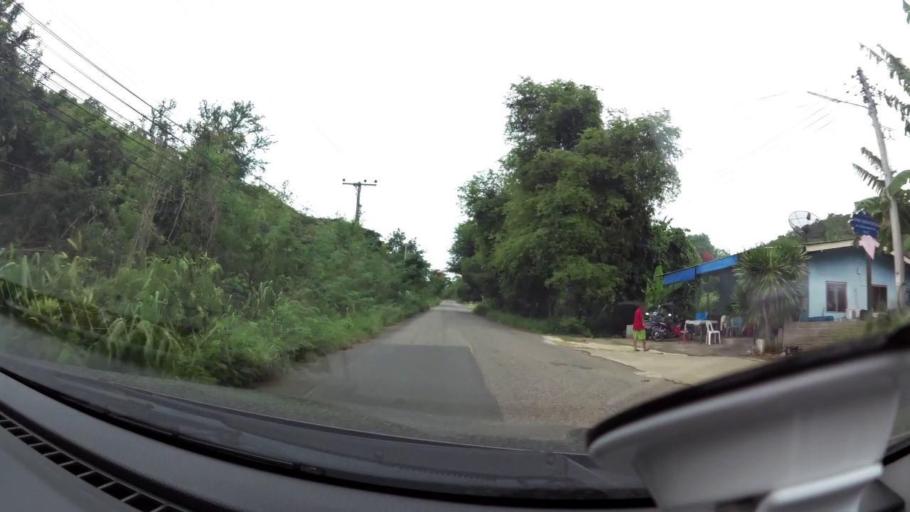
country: TH
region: Prachuap Khiri Khan
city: Pran Buri
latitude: 12.4410
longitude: 99.9701
